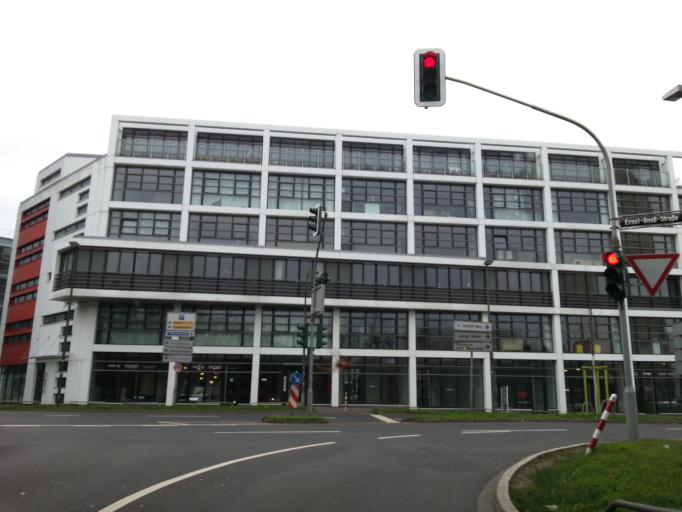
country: DE
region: North Rhine-Westphalia
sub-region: Regierungsbezirk Dusseldorf
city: Dusseldorf
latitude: 51.2163
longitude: 6.7607
